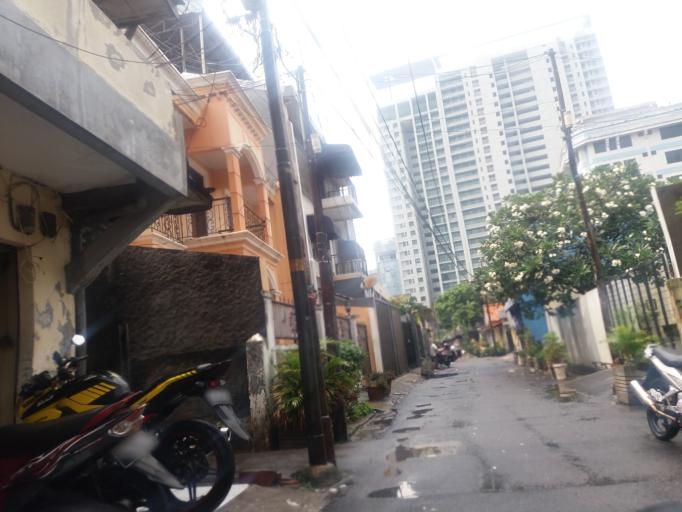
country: ID
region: Jakarta Raya
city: Jakarta
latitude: -6.2169
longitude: 106.8271
